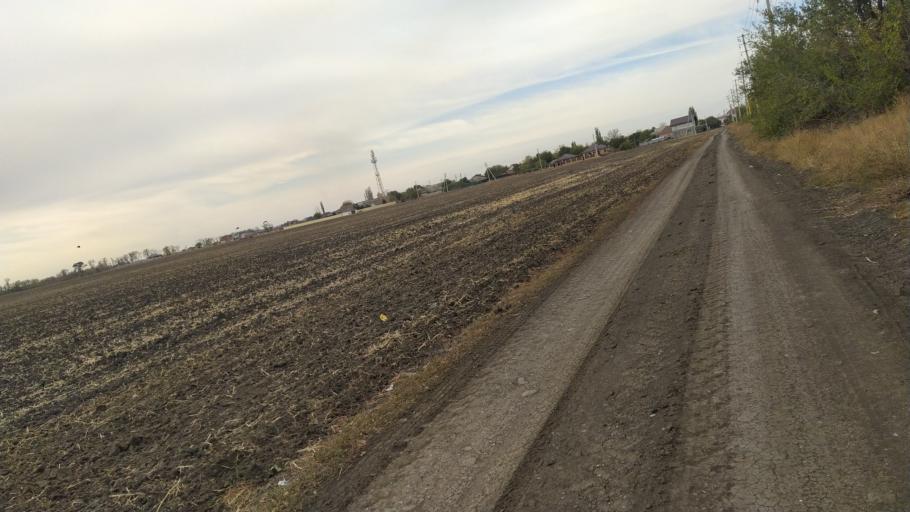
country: RU
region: Rostov
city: Bataysk
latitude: 47.1106
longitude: 39.6819
